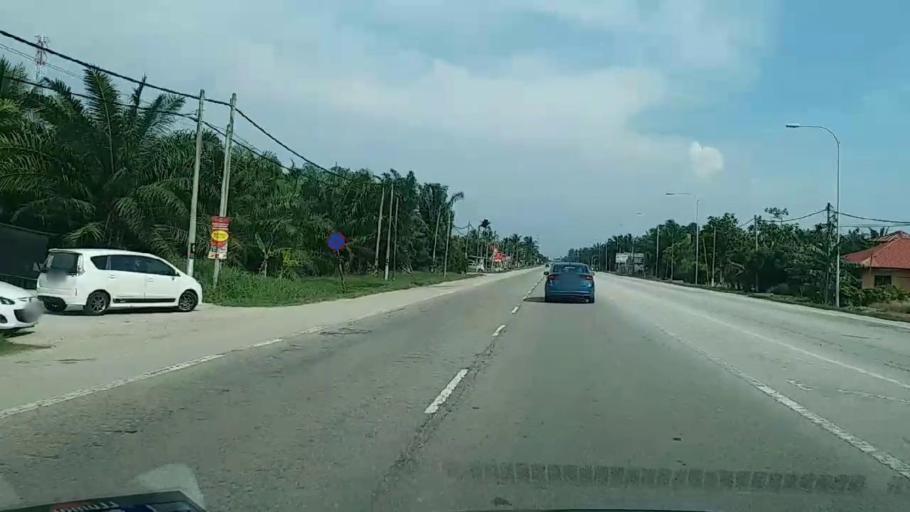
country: MY
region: Selangor
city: Kuala Selangor
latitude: 3.3727
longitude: 101.2397
